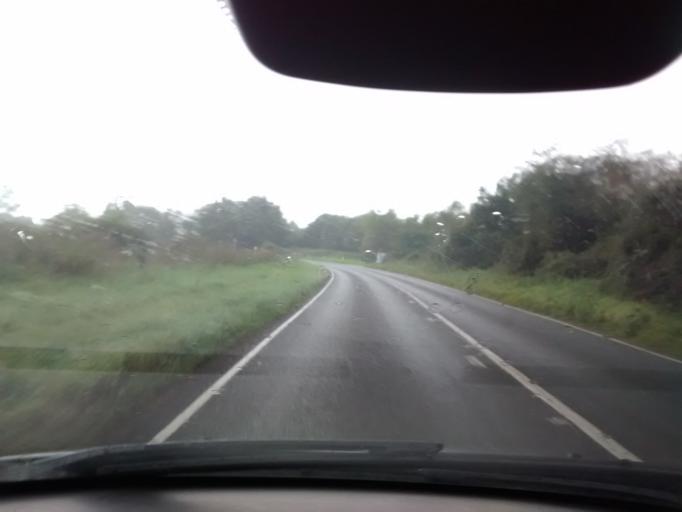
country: GB
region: England
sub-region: Hampshire
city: Fordingbridge
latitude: 50.9005
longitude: -1.7815
